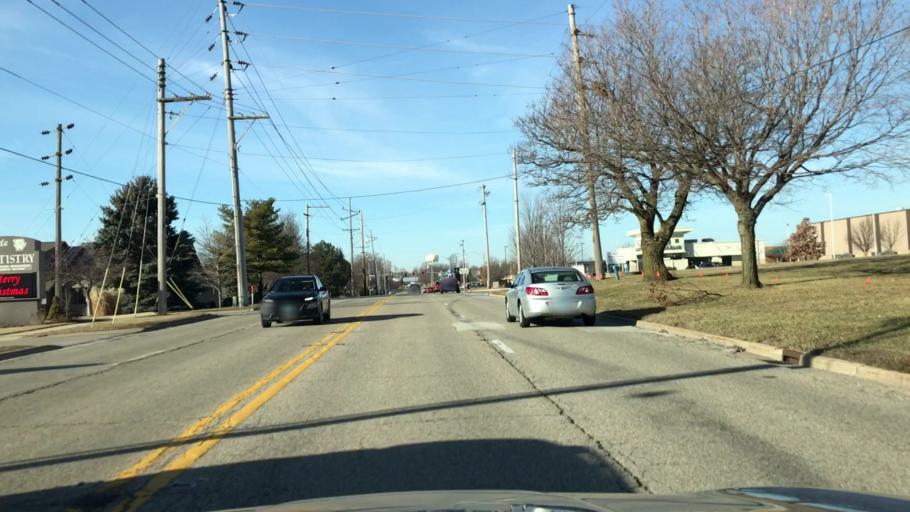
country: US
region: Illinois
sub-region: McLean County
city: Normal
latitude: 40.5177
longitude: -88.9575
